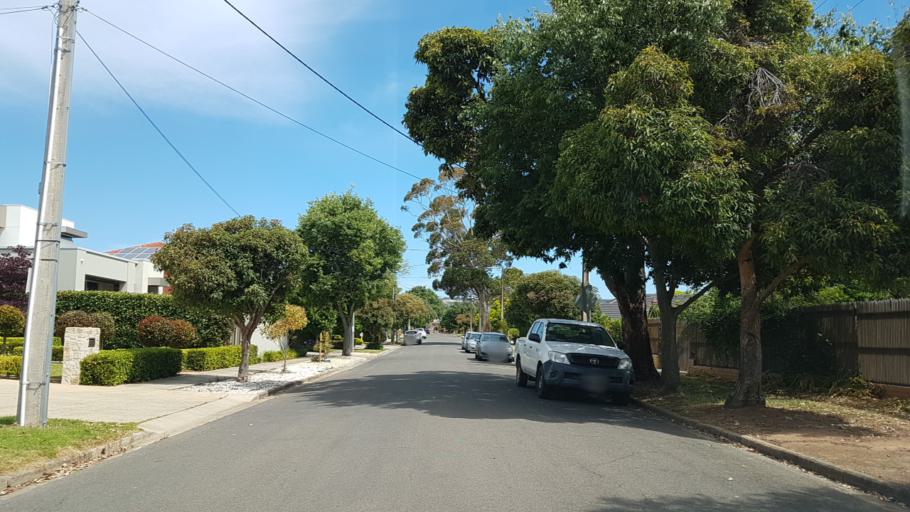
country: AU
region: South Australia
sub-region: Burnside
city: Kensington Gardens
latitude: -34.9114
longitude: 138.6650
